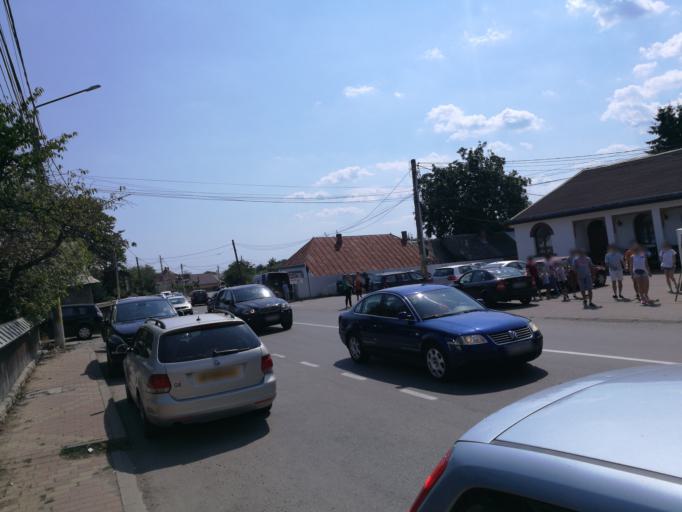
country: RO
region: Neamt
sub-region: Oras Targu Neamt
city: Humulesti
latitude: 47.1978
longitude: 26.3551
